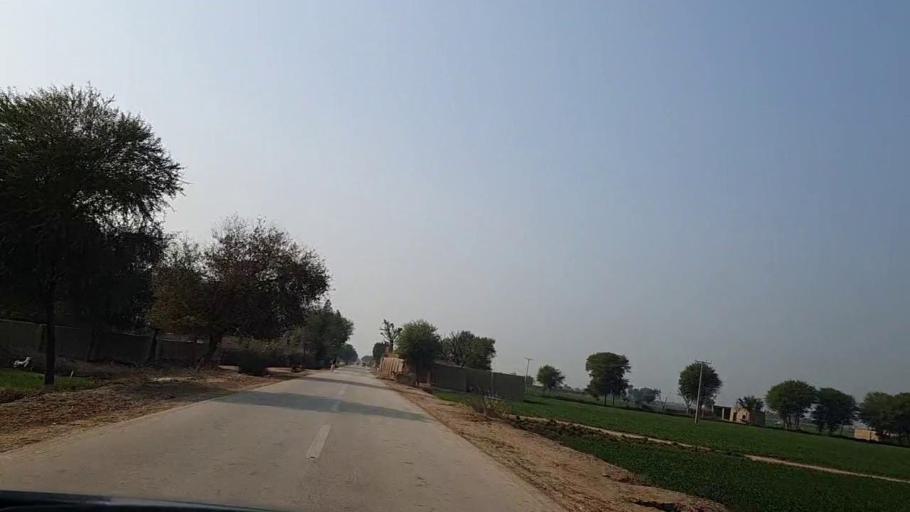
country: PK
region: Sindh
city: Sann
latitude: 26.1423
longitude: 68.1526
